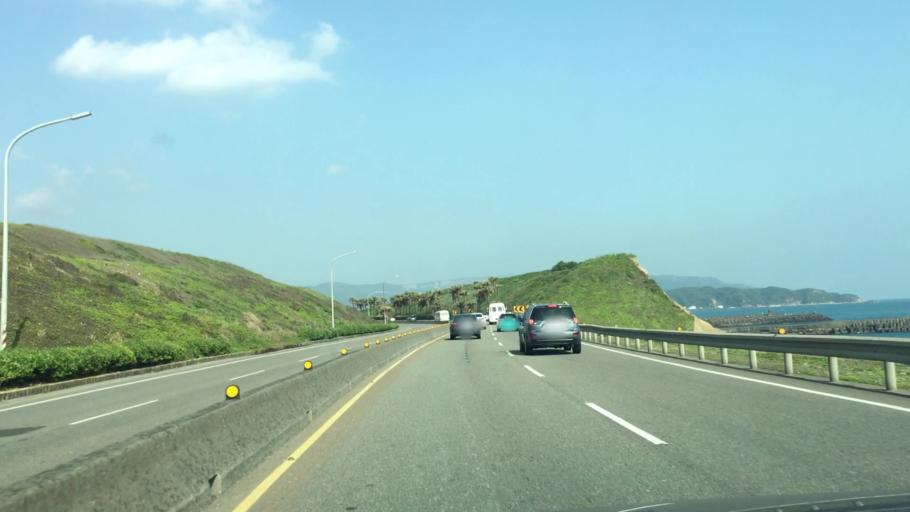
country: TW
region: Taiwan
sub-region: Keelung
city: Keelung
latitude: 25.2041
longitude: 121.6673
